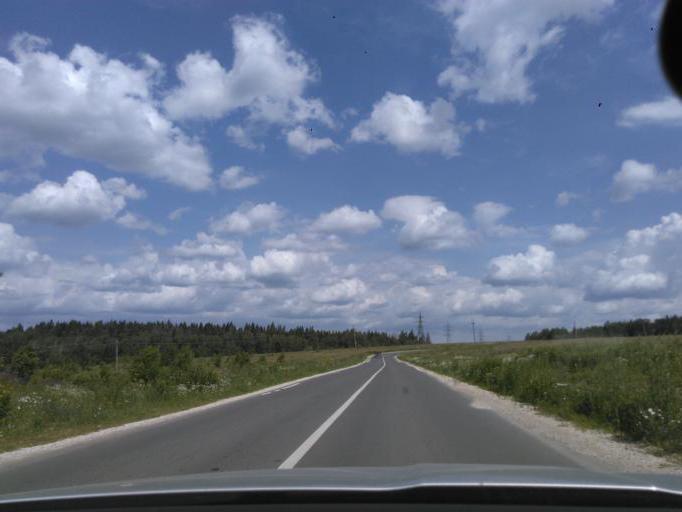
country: RU
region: Moskovskaya
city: Solnechnogorsk
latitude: 56.1350
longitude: 36.9716
